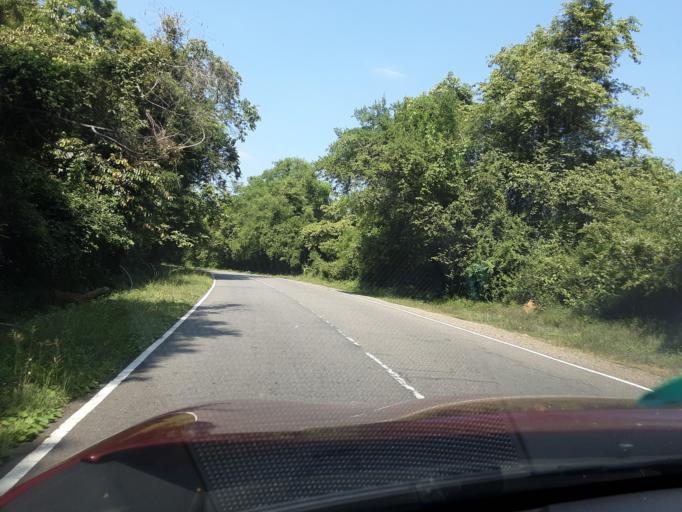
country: LK
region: Uva
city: Badulla
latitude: 7.2726
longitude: 81.0513
